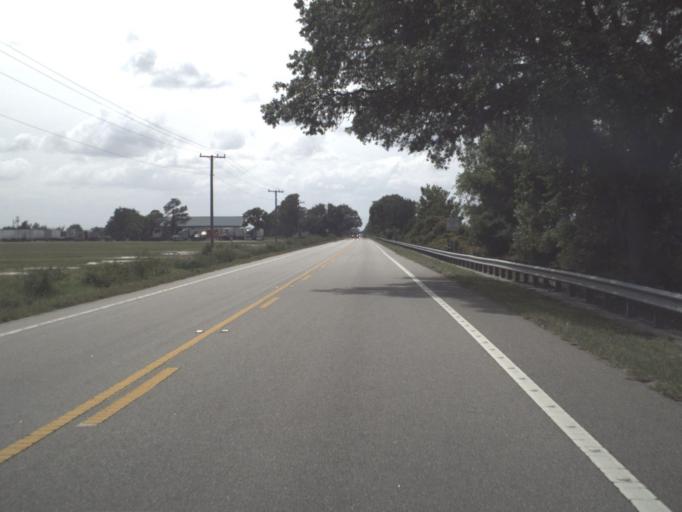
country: US
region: Florida
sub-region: Flagler County
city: Bunnell
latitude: 29.4823
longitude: -81.3518
